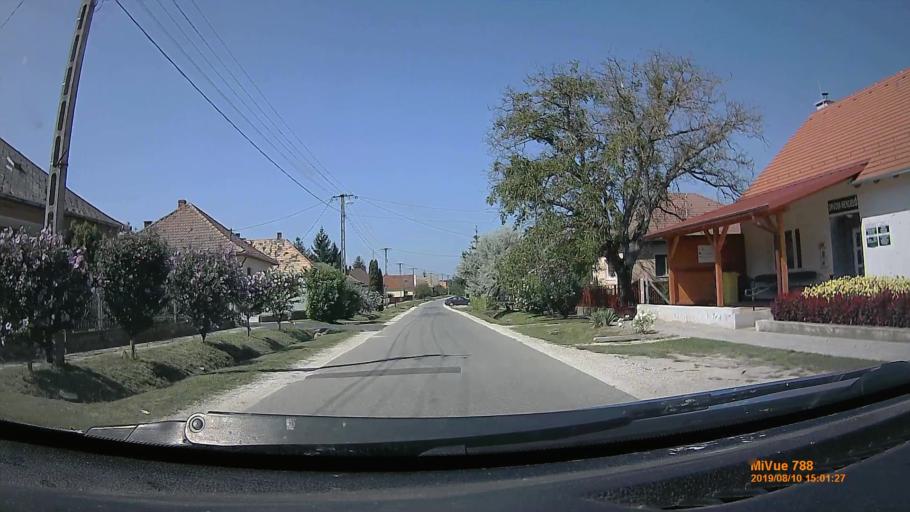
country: HU
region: Somogy
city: Lengyeltoti
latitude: 46.6491
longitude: 17.5771
